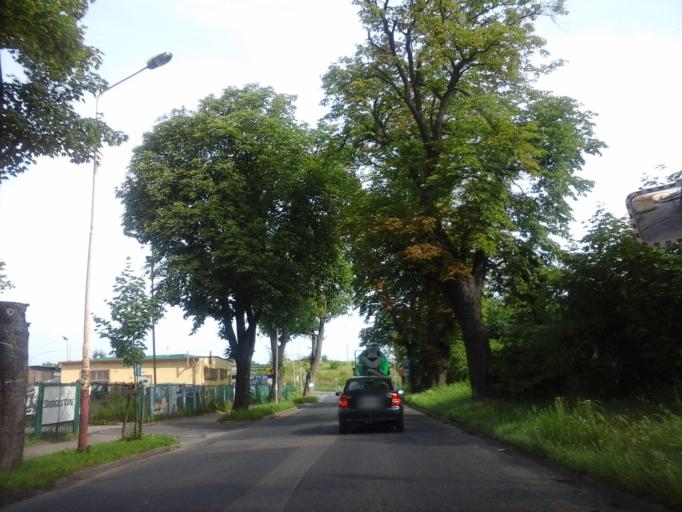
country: PL
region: West Pomeranian Voivodeship
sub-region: Powiat stargardzki
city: Stargard Szczecinski
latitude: 53.3264
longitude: 15.0396
